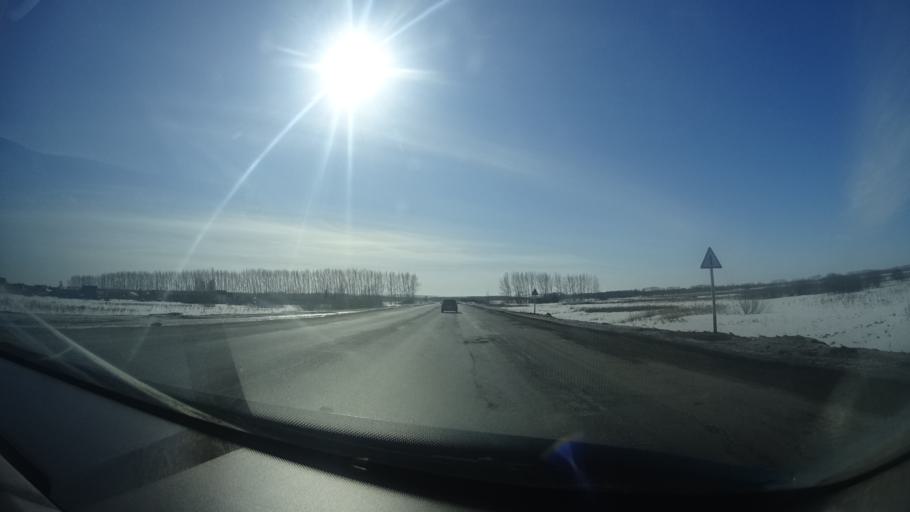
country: RU
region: Bashkortostan
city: Mikhaylovka
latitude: 54.9265
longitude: 55.7394
